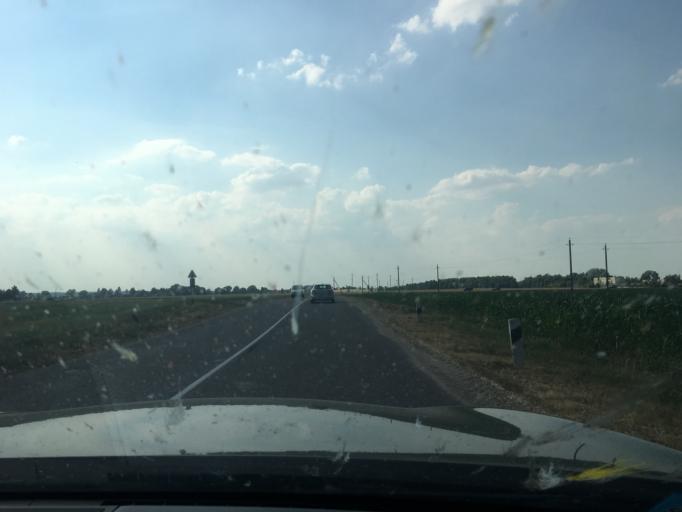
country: BY
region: Grodnenskaya
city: Svislach
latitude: 53.0223
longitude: 24.0913
